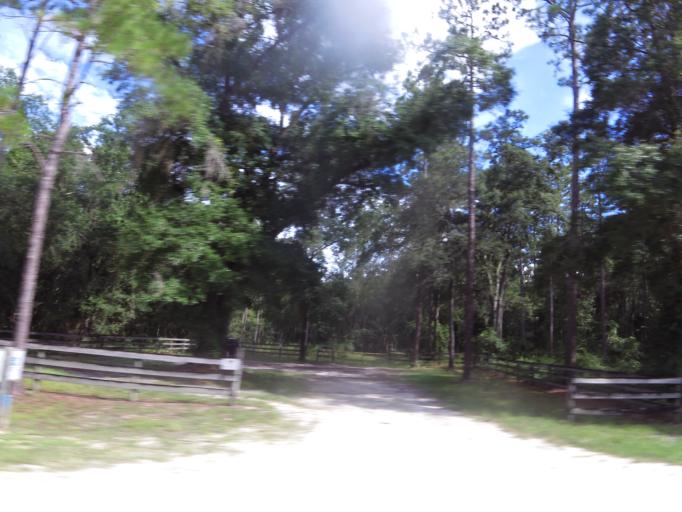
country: US
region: Florida
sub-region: Clay County
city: Green Cove Springs
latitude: 29.9357
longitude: -81.6662
